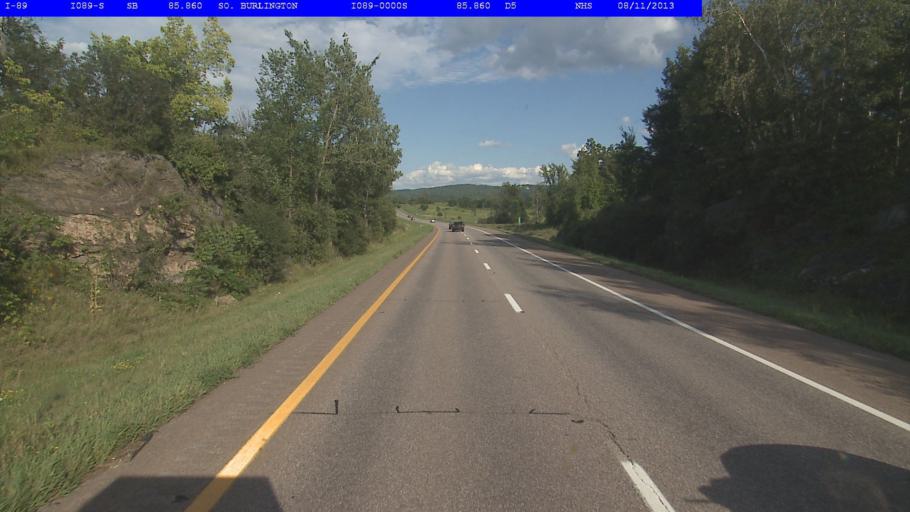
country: US
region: Vermont
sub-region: Chittenden County
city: South Burlington
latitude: 44.4463
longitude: -73.1518
